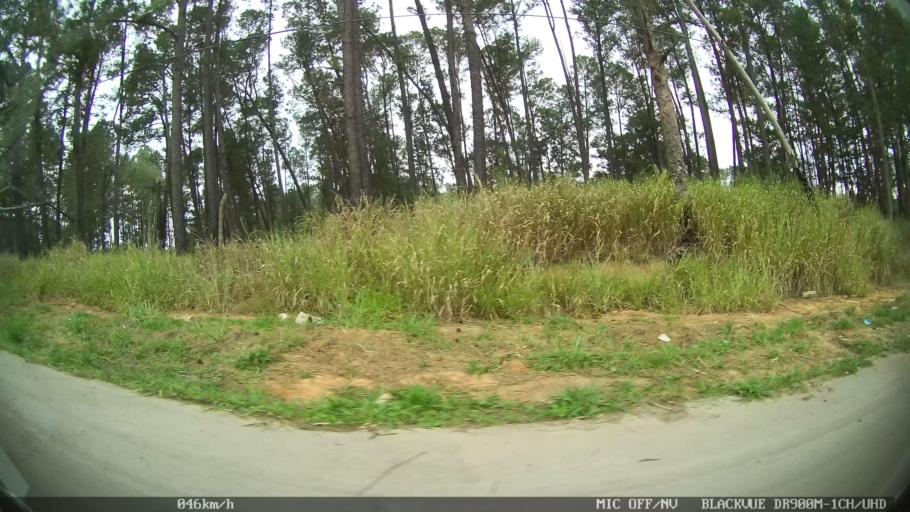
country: BR
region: Sao Paulo
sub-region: Santa Barbara D'Oeste
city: Santa Barbara d'Oeste
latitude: -22.6991
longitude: -47.3855
